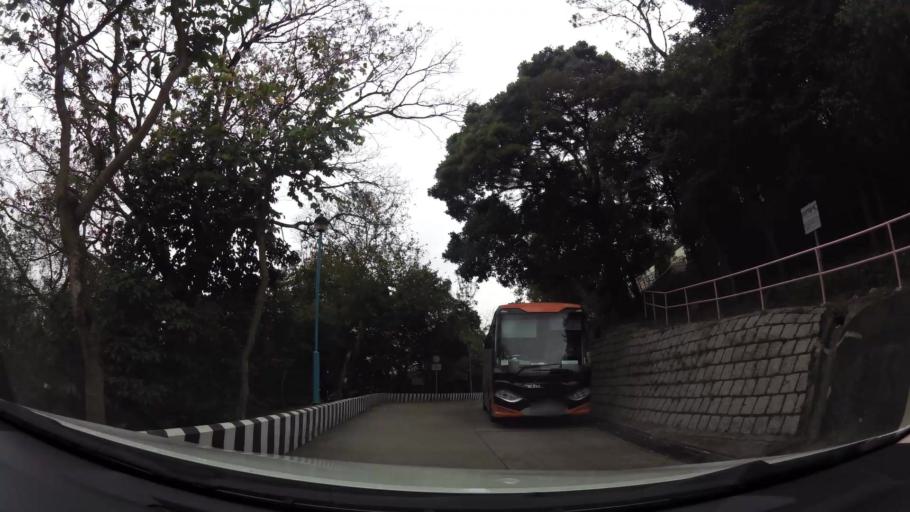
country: HK
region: Wanchai
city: Wan Chai
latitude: 22.2760
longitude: 114.2319
